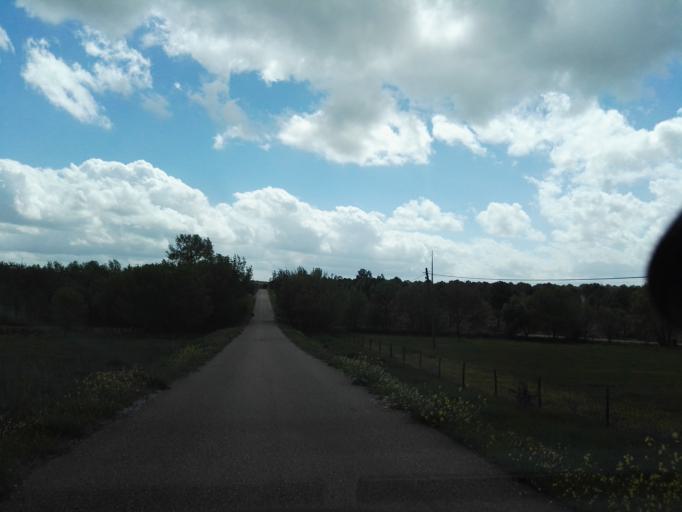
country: PT
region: Portalegre
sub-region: Elvas
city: Elvas
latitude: 38.9760
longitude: -7.1747
